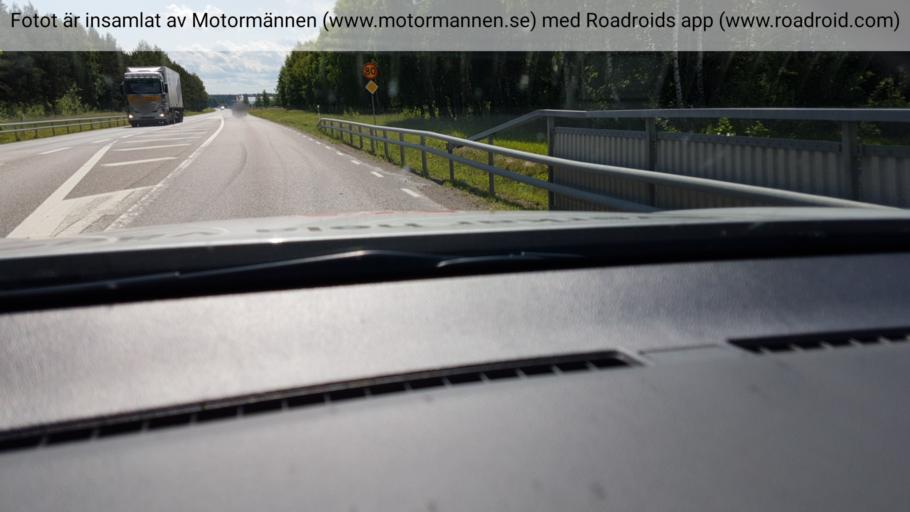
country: SE
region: Vaestra Goetaland
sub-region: Lidkopings Kommun
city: Lidkoping
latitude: 58.5103
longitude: 13.1187
